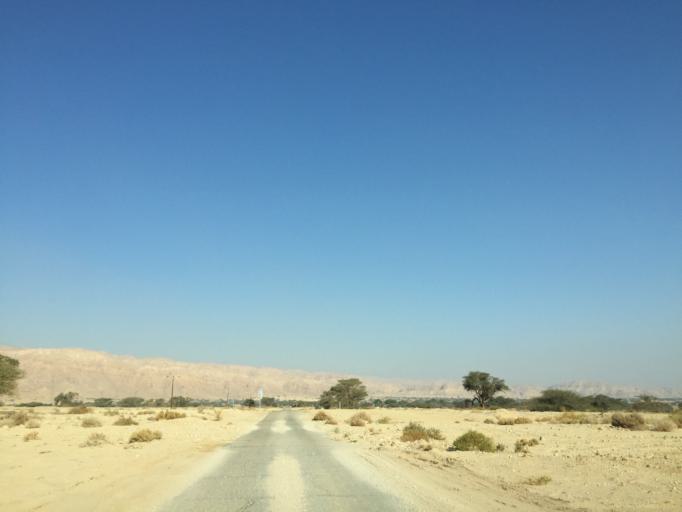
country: JO
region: Ma'an
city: Al Quwayrah
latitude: 29.8398
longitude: 35.0306
